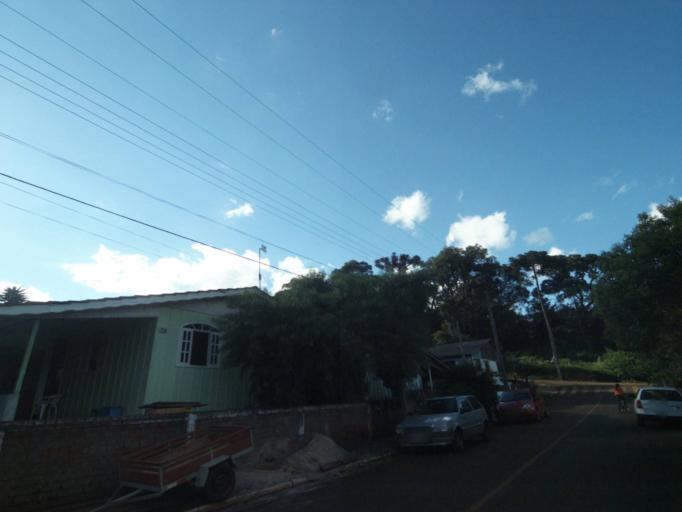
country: BR
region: Parana
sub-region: Uniao Da Vitoria
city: Uniao da Vitoria
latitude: -26.1598
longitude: -51.5351
